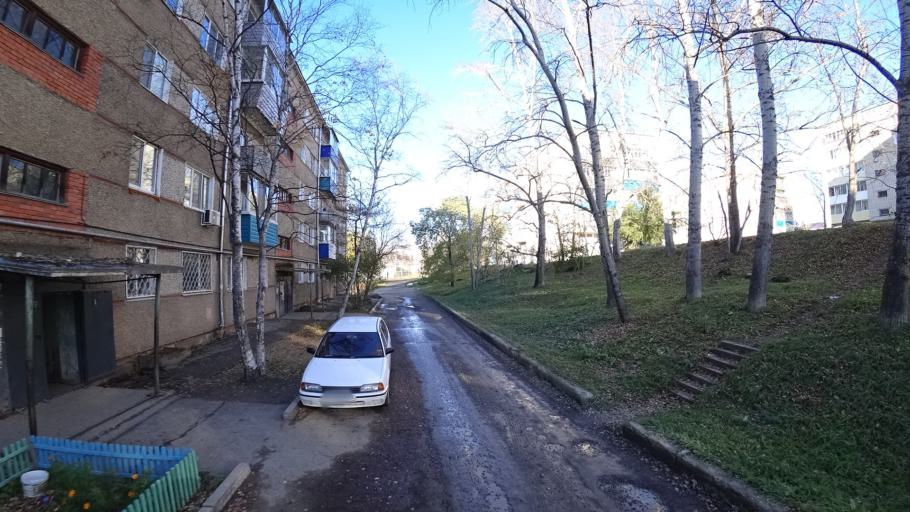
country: RU
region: Khabarovsk Krai
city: Amursk
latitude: 50.2312
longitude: 136.9114
